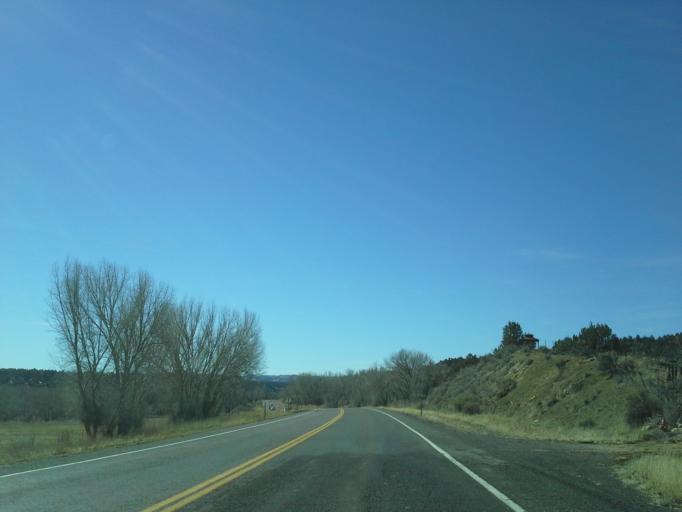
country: US
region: Utah
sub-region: Kane County
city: Kanab
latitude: 37.2580
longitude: -112.6583
